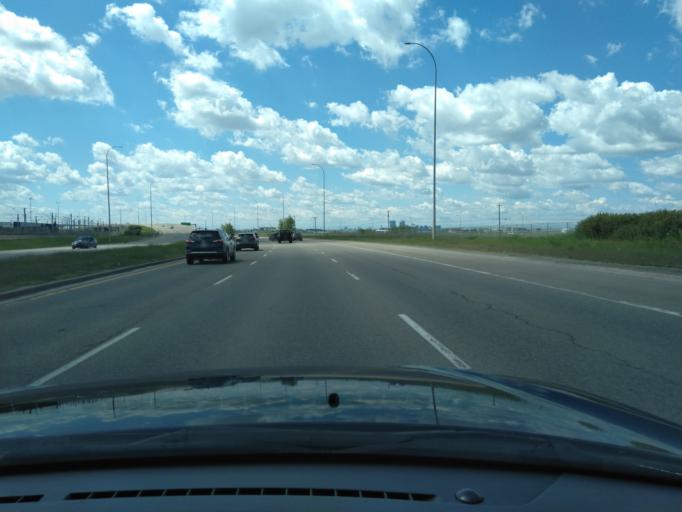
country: CA
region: Alberta
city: Calgary
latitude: 51.1067
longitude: -113.9797
